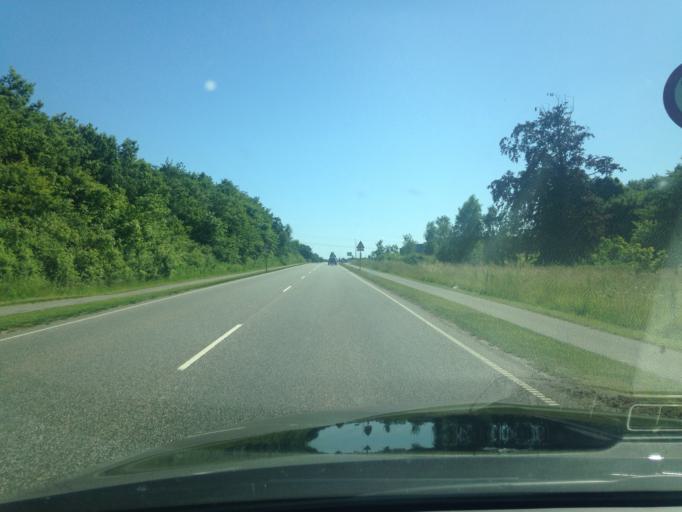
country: DK
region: South Denmark
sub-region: Kolding Kommune
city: Kolding
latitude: 55.5367
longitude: 9.4716
